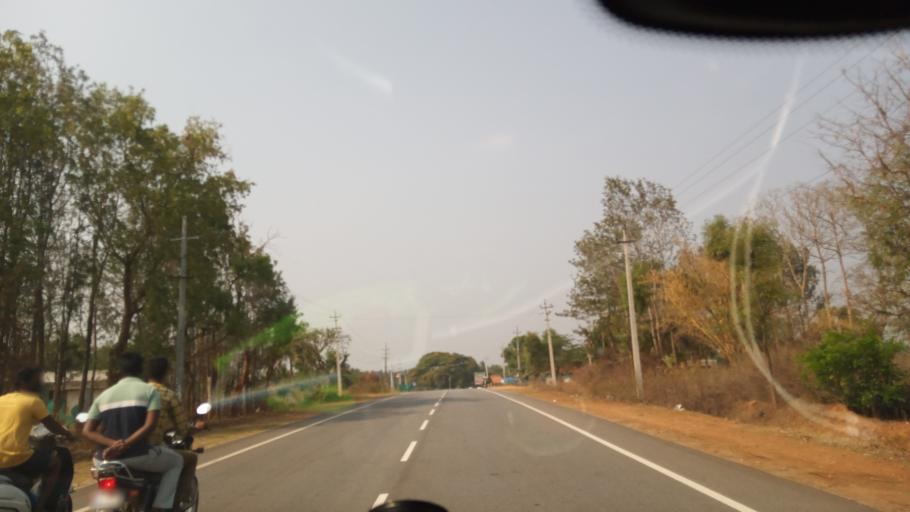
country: IN
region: Karnataka
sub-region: Mandya
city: Melukote
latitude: 12.6959
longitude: 76.6972
